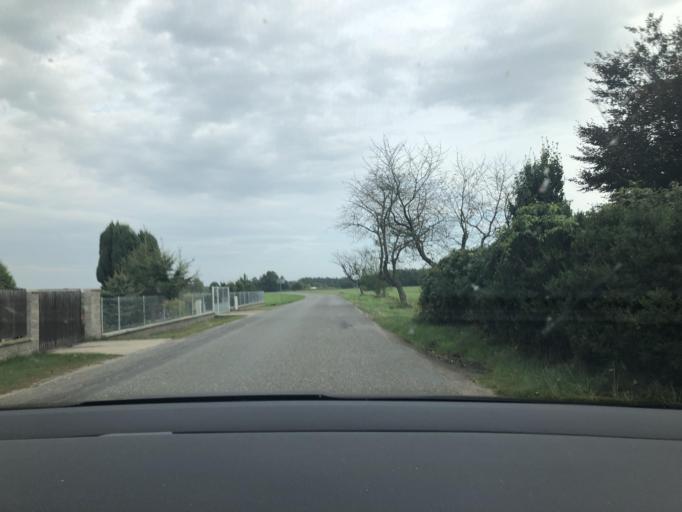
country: CZ
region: Pardubicky
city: Recany nad Labem
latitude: 50.0797
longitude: 15.4471
